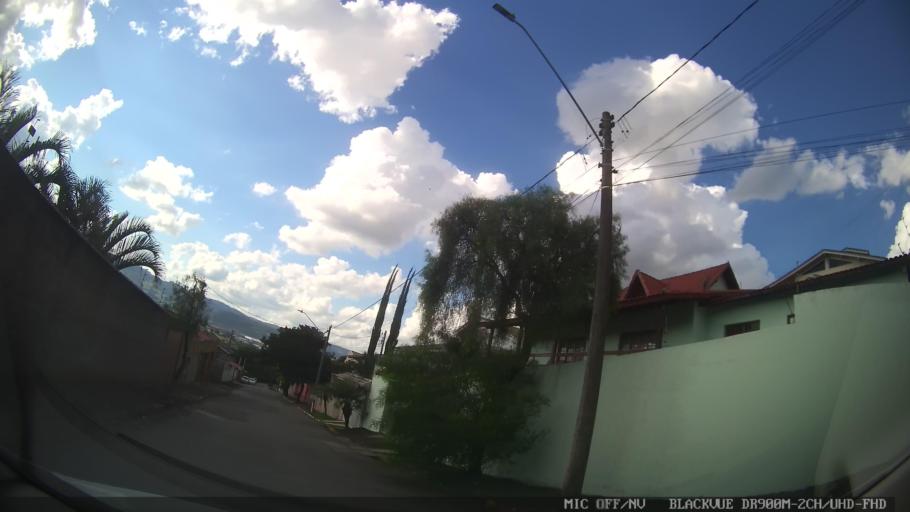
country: BR
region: Minas Gerais
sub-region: Extrema
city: Extrema
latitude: -22.8613
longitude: -46.3177
